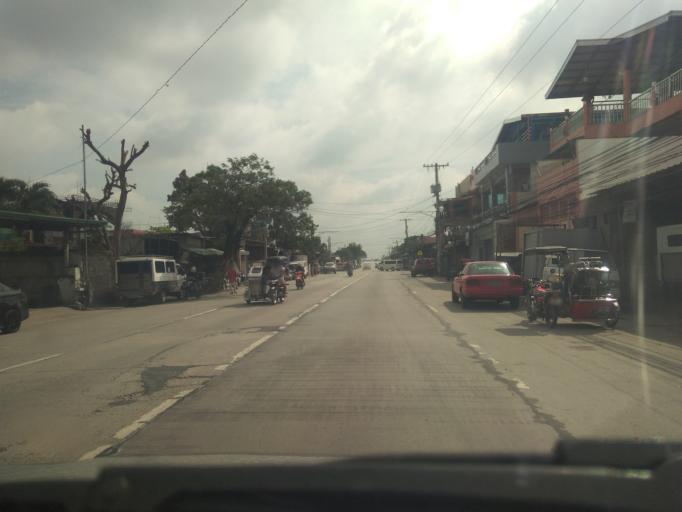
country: PH
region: Central Luzon
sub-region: Province of Pampanga
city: Santo Domingo
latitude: 15.0012
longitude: 120.7263
